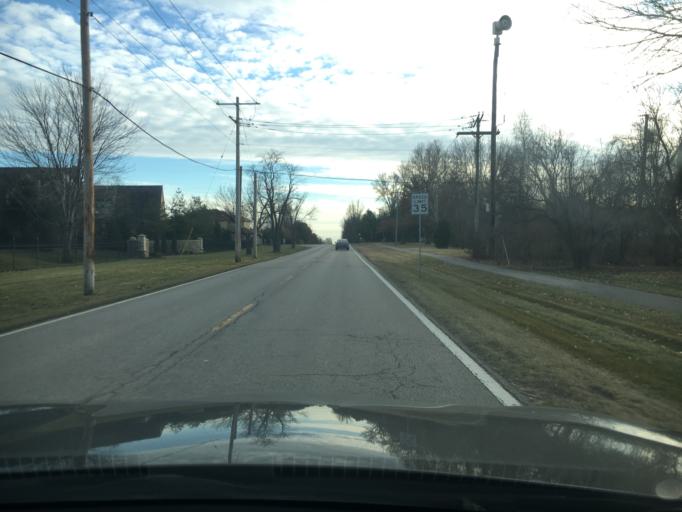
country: US
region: Kansas
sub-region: Johnson County
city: Leawood
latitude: 38.8771
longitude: -94.6306
